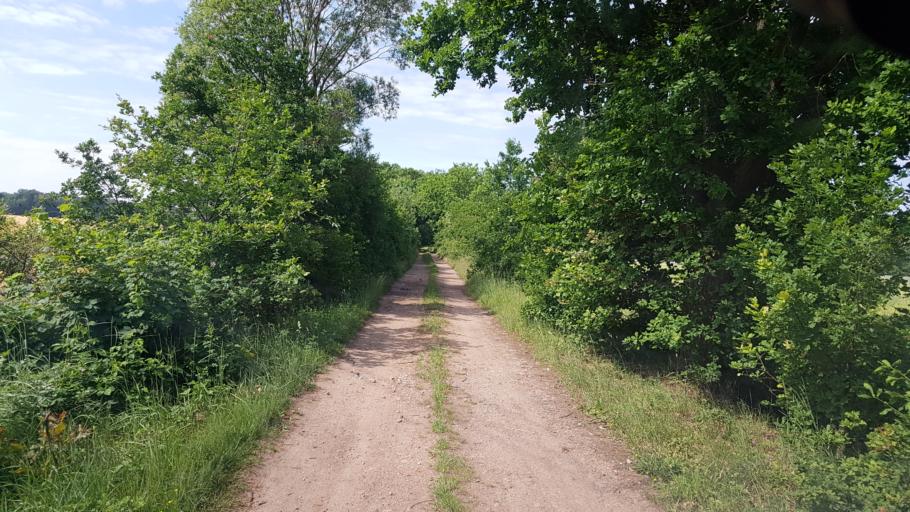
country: DE
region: Brandenburg
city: Doberlug-Kirchhain
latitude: 51.6196
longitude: 13.5303
